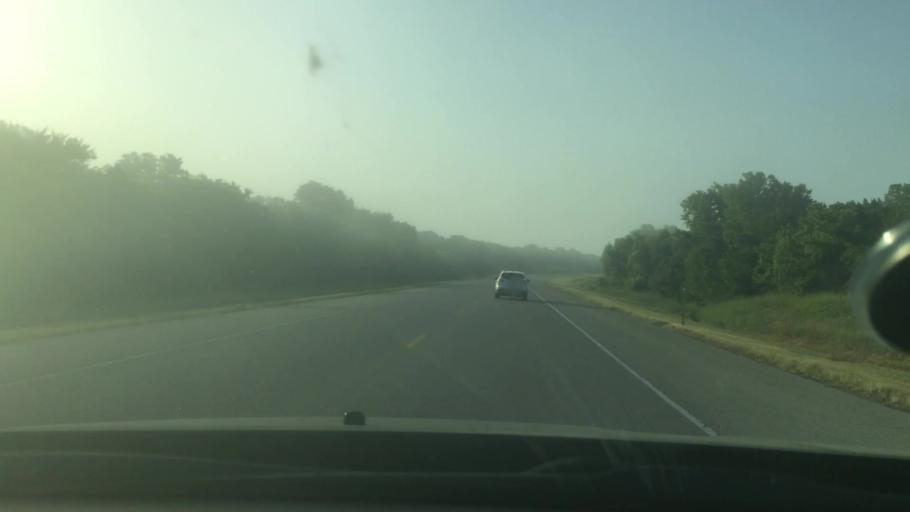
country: US
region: Oklahoma
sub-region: Pontotoc County
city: Ada
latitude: 34.7038
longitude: -96.6067
